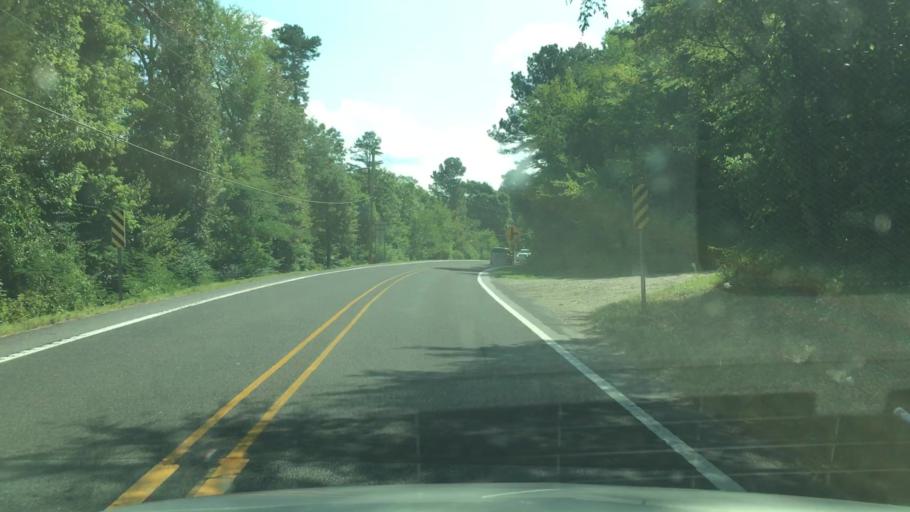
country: US
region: Arkansas
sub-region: Garland County
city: Piney
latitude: 34.5096
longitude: -93.1740
